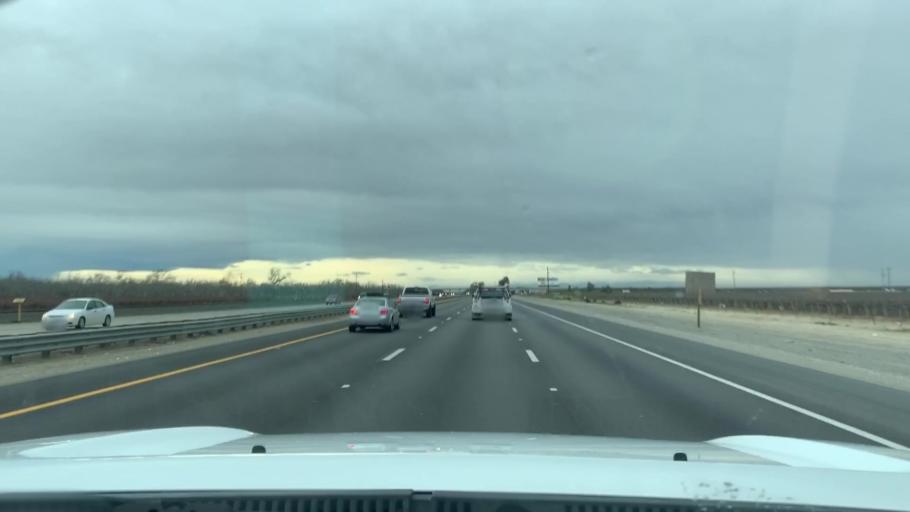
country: US
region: California
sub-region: Kern County
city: McFarland
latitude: 35.6561
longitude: -119.2222
